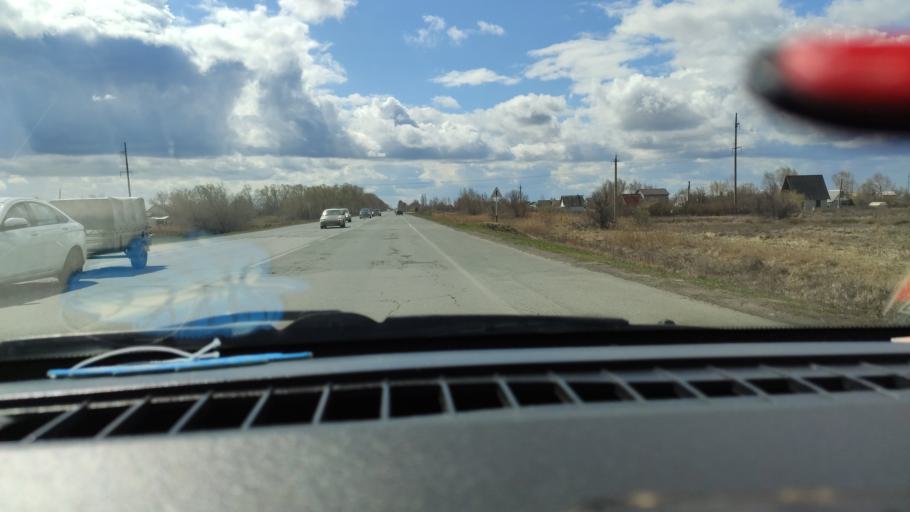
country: RU
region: Samara
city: Tol'yatti
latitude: 53.7069
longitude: 49.4224
